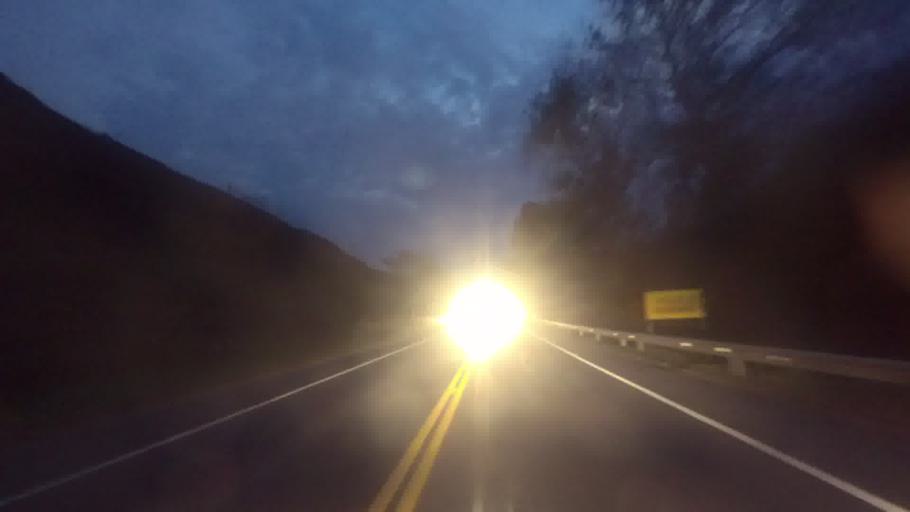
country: BR
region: Rio de Janeiro
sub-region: Sapucaia
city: Sapucaia
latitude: -21.9587
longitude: -42.8562
